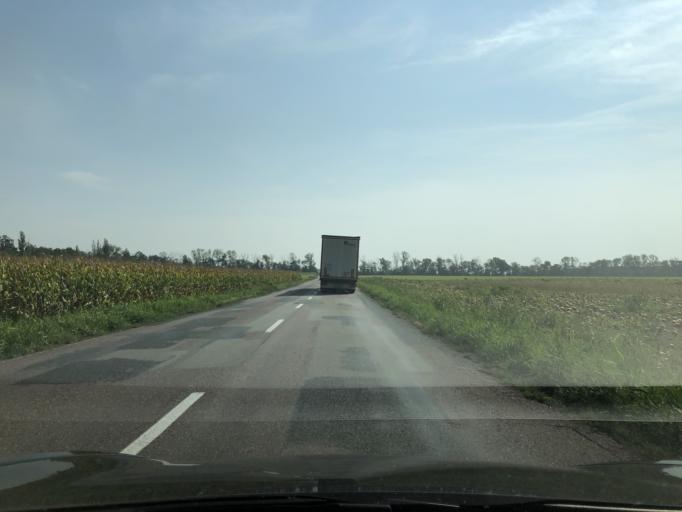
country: CZ
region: South Moravian
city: Brezi
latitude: 48.8252
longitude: 16.5409
